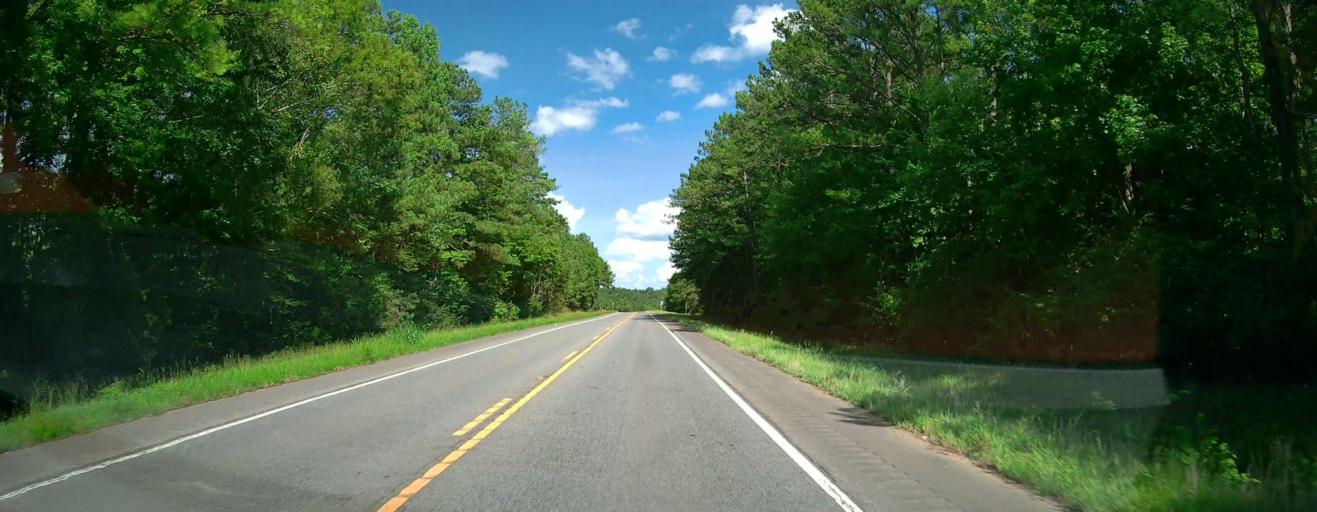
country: US
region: Alabama
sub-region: Pickens County
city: Gordo
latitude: 33.2857
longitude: -87.8564
